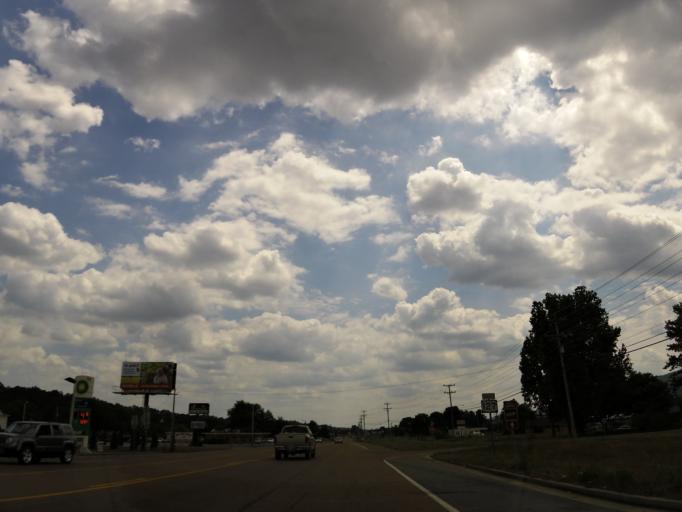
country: US
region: Tennessee
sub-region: Sequatchie County
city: Dunlap
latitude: 35.3928
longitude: -85.3757
